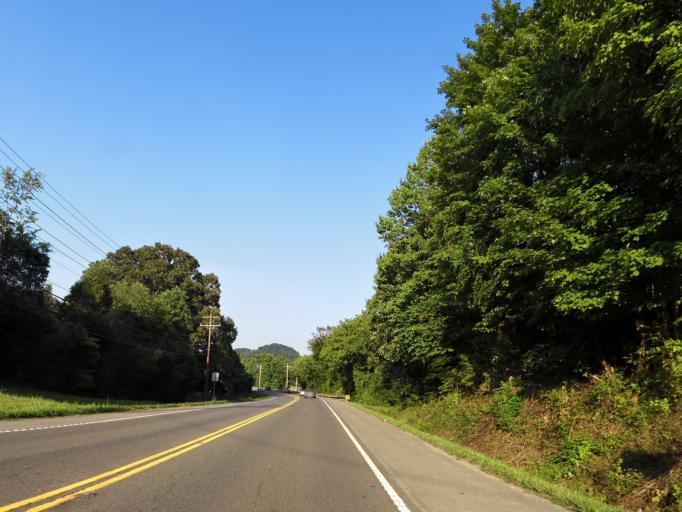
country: US
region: Tennessee
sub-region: Anderson County
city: Clinton
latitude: 36.0374
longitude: -84.1208
